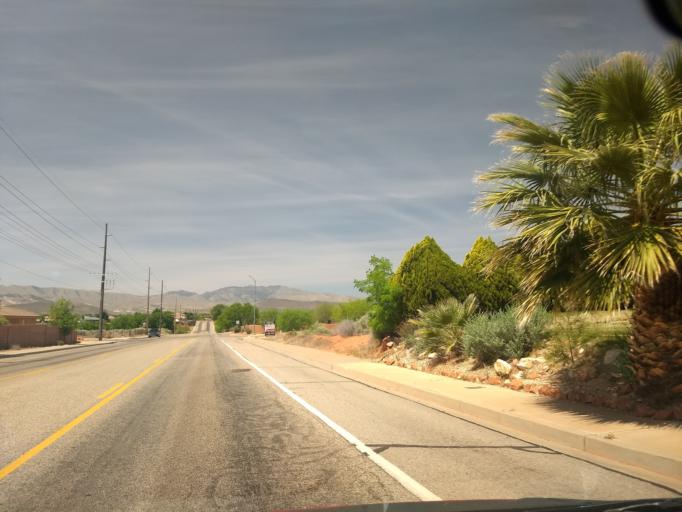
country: US
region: Utah
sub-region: Washington County
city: Santa Clara
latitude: 37.1430
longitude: -113.6298
